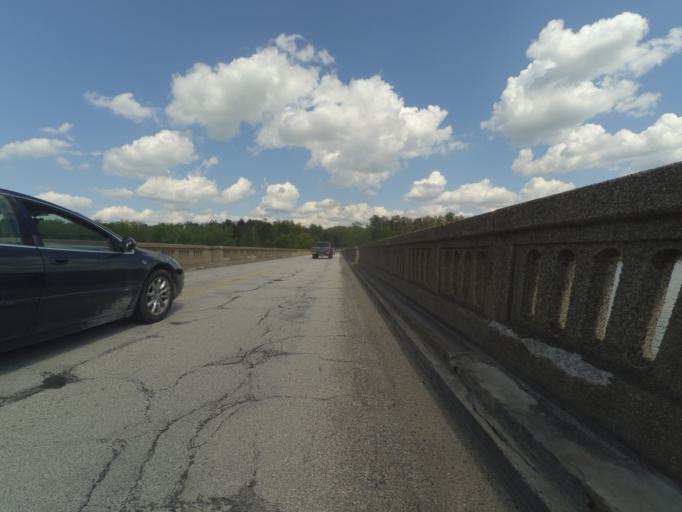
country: US
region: Ohio
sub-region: Trumbull County
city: Mineral Ridge
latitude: 41.1354
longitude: -80.7929
